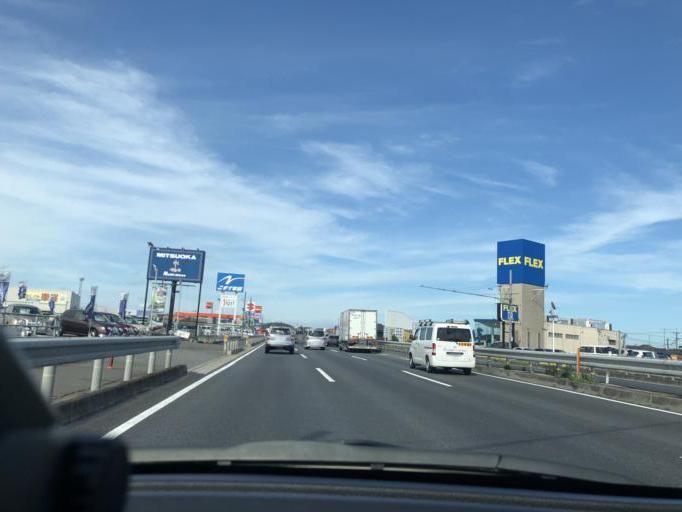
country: JP
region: Okayama
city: Kurashiki
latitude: 34.5929
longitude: 133.8010
